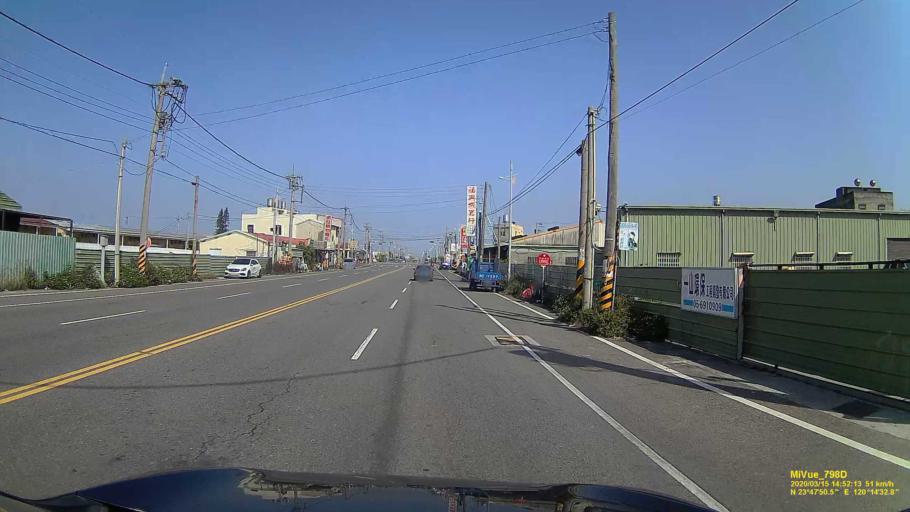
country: TW
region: Taiwan
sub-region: Yunlin
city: Douliu
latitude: 23.7973
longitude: 120.2427
